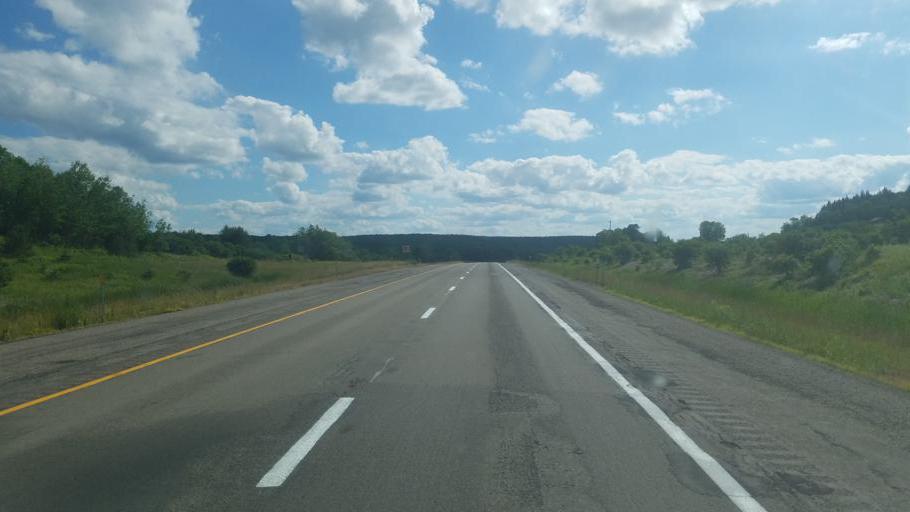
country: US
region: New York
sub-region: Allegany County
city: Alfred
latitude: 42.3104
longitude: -77.8649
